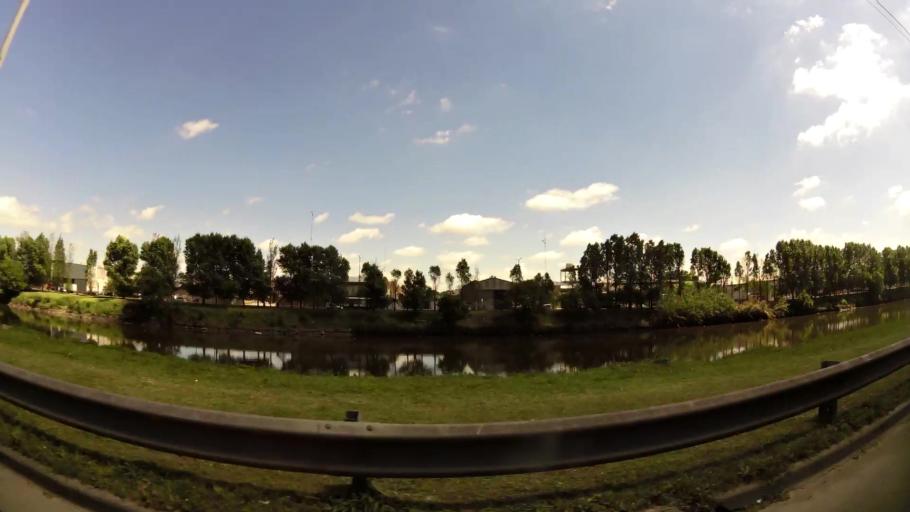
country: AR
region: Buenos Aires
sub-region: Partido de Lanus
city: Lanus
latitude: -34.6627
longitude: -58.4234
